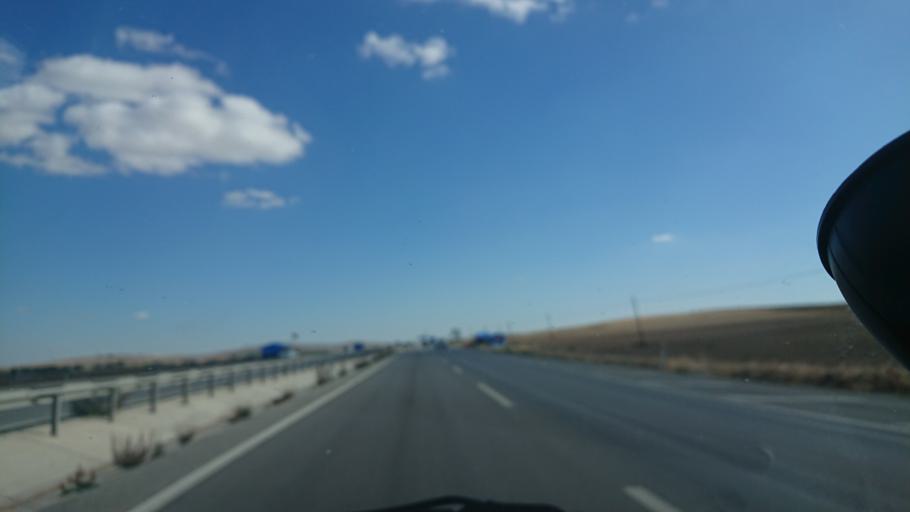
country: TR
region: Eskisehir
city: Mahmudiye
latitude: 39.5252
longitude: 30.9549
